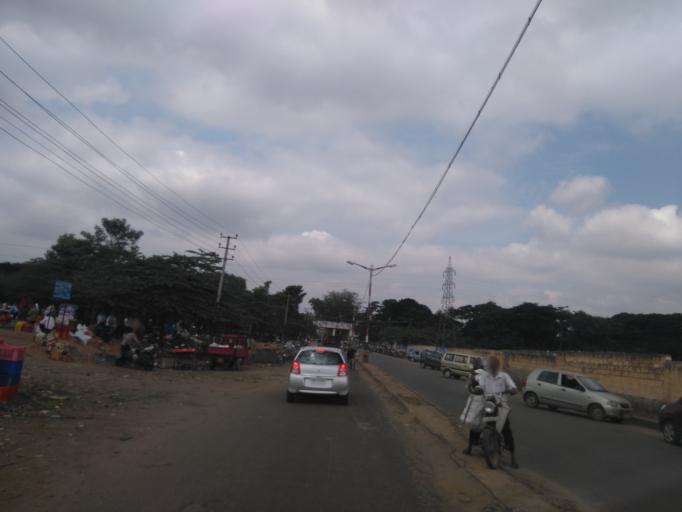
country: IN
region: Karnataka
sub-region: Mysore
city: Mysore
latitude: 12.2977
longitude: 76.6597
